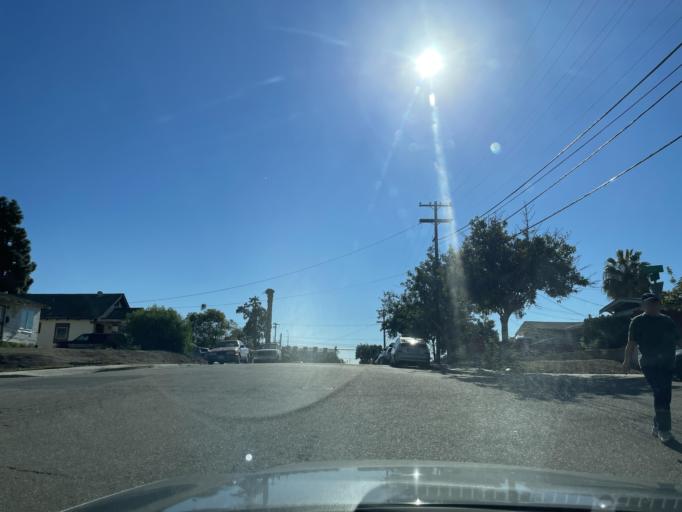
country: US
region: California
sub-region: San Diego County
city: National City
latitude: 32.6716
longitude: -117.0985
